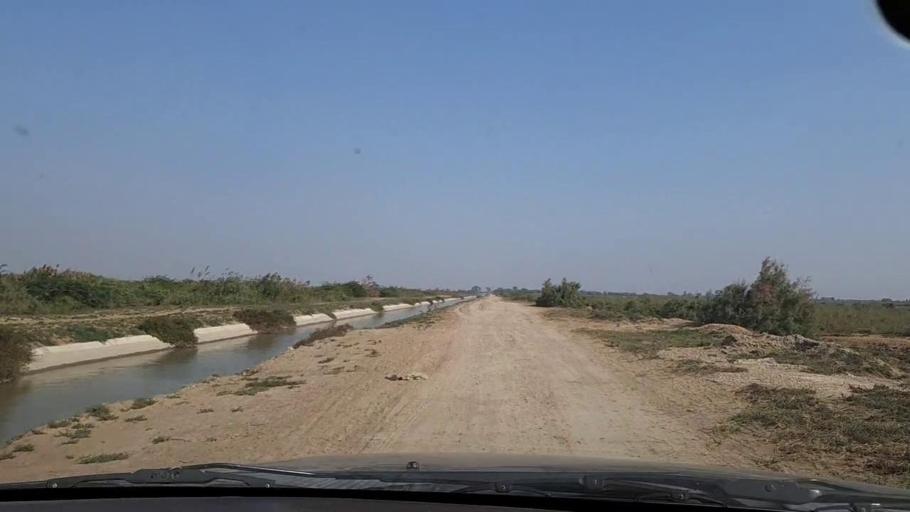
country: PK
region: Sindh
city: Mirpur Sakro
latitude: 24.3420
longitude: 67.7193
